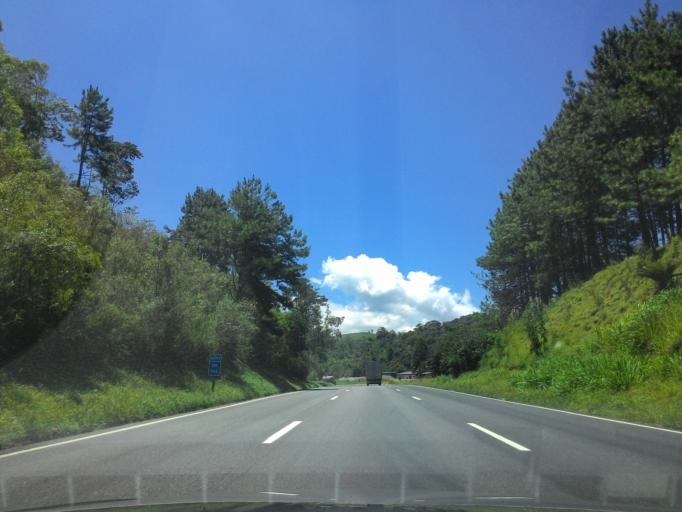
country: BR
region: Parana
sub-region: Antonina
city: Antonina
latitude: -25.0475
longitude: -48.5454
